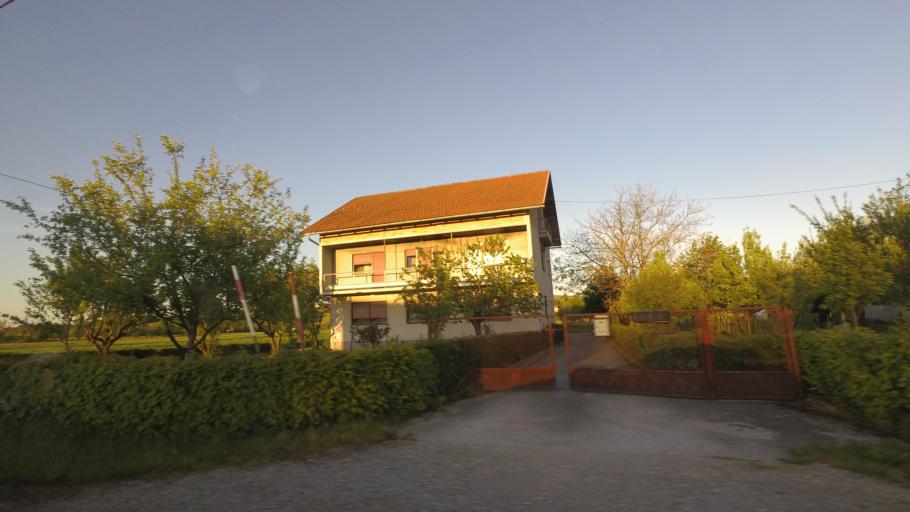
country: HR
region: Karlovacka
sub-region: Grad Karlovac
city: Karlovac
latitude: 45.4509
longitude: 15.5608
